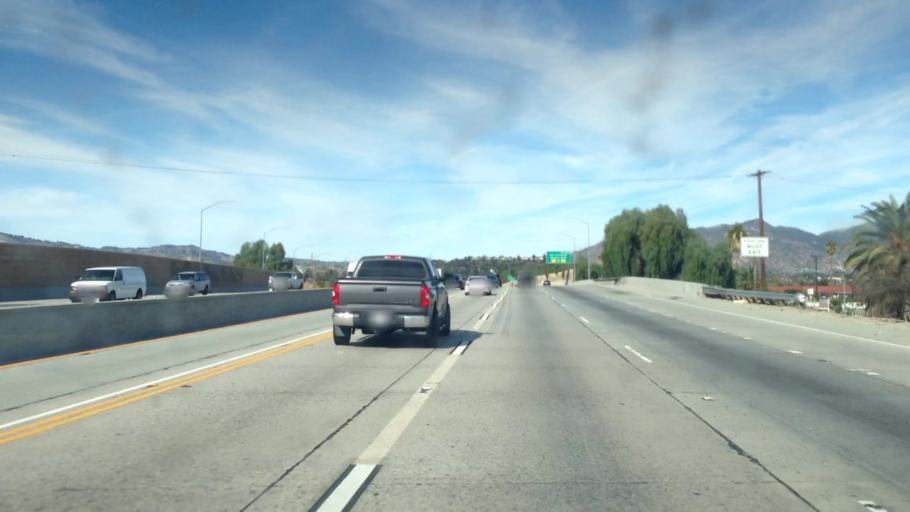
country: US
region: California
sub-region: Los Angeles County
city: San Fernando
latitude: 34.2719
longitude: -118.4521
